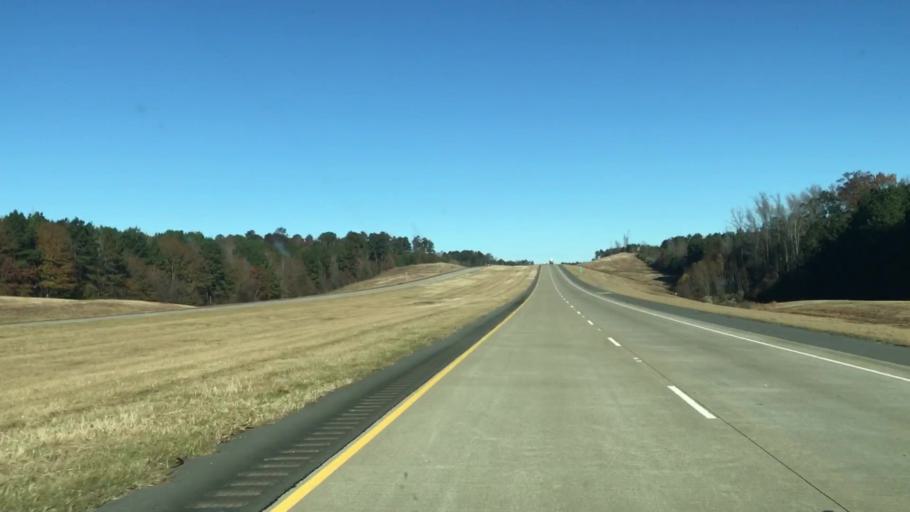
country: US
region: Louisiana
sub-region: Caddo Parish
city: Vivian
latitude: 32.9653
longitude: -93.9048
